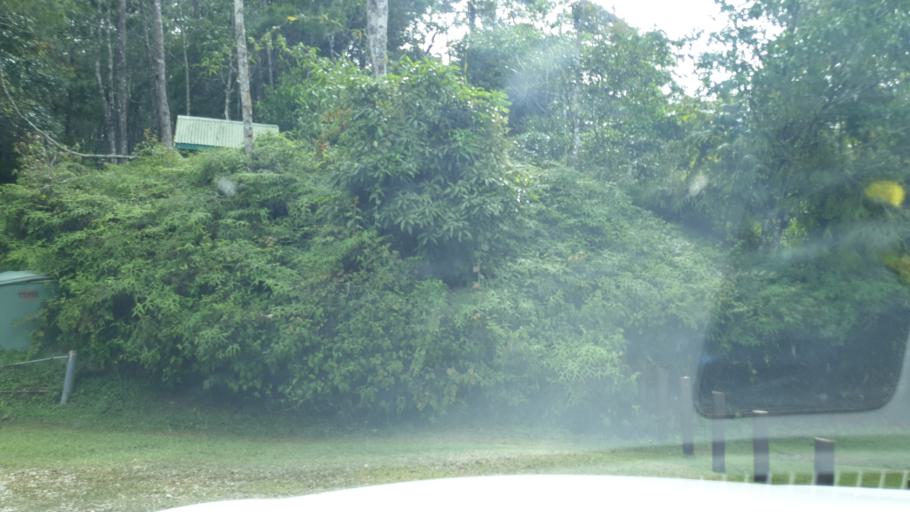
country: PG
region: National Capital
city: Port Moresby
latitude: -9.4356
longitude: 147.3642
